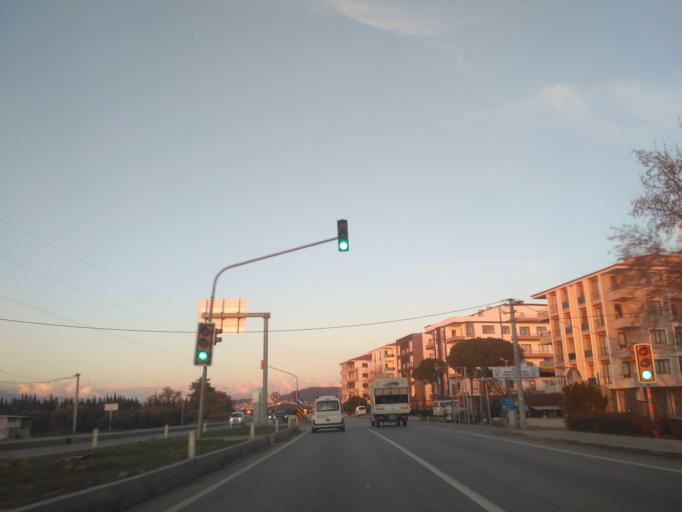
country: TR
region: Balikesir
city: Emrutabat
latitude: 39.3947
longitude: 26.8420
